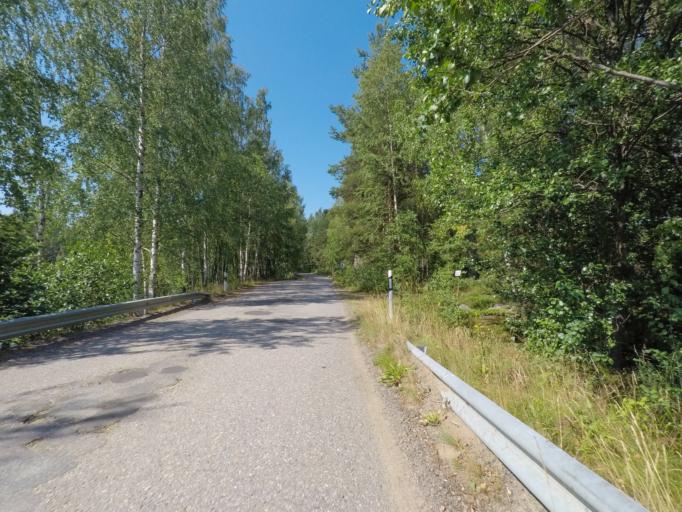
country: FI
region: Southern Savonia
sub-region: Mikkeli
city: Puumala
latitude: 61.4062
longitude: 28.0638
